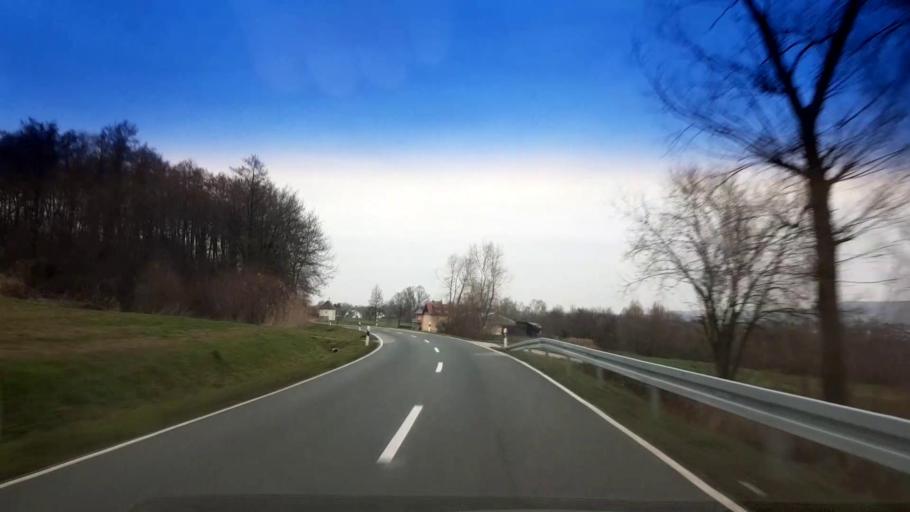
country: DE
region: Bavaria
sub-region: Upper Franconia
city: Altendorf
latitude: 49.7851
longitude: 11.0066
